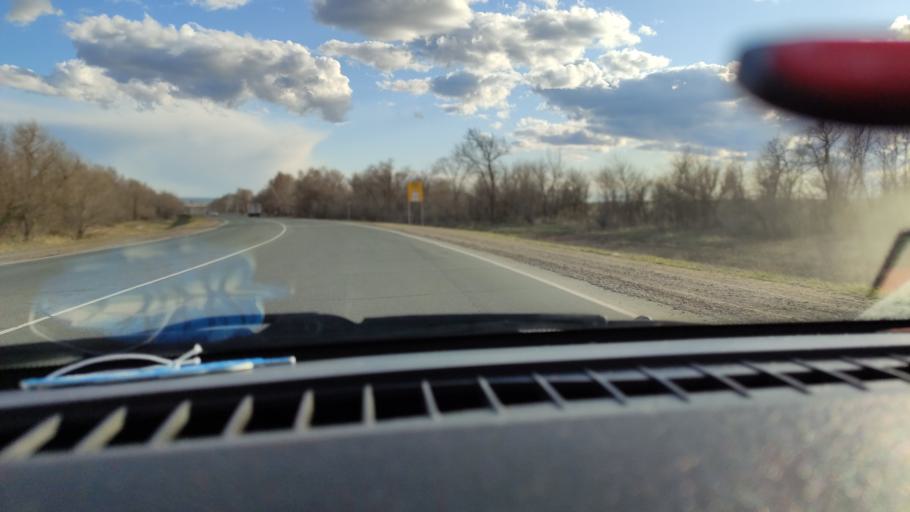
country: RU
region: Saratov
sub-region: Saratovskiy Rayon
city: Saratov
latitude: 51.7037
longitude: 46.0128
